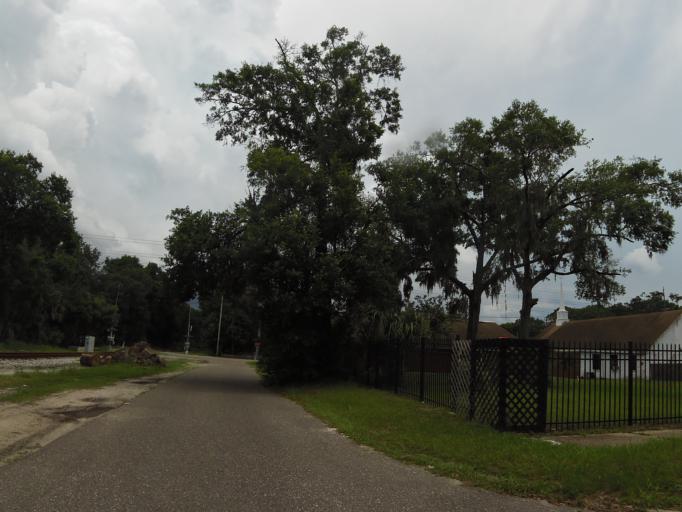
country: US
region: Florida
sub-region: Duval County
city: Jacksonville
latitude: 30.3734
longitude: -81.6459
